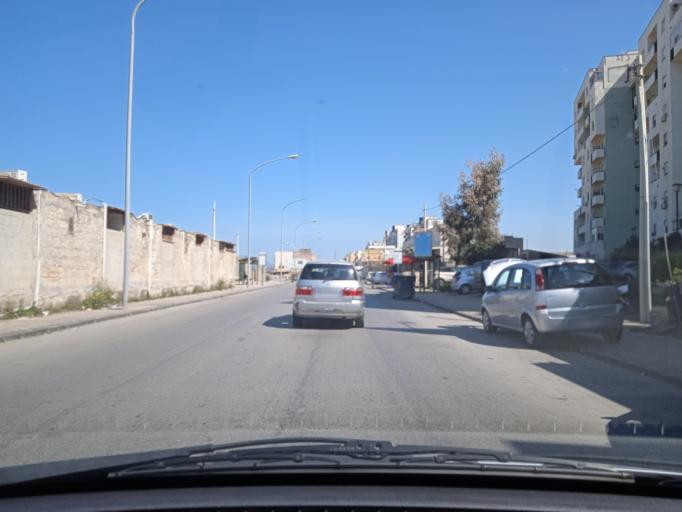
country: IT
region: Sicily
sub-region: Palermo
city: Ciaculli
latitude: 38.0981
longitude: 13.4105
